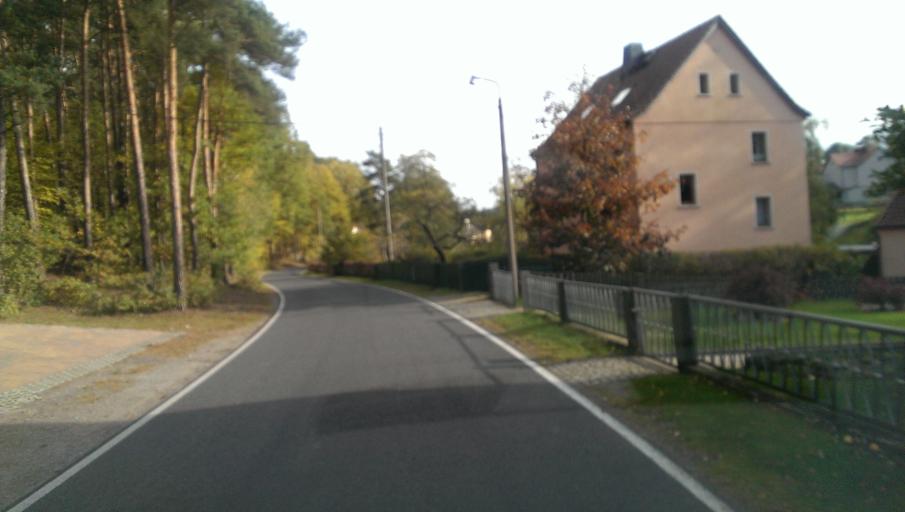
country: DE
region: Saxony
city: Konigsbruck
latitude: 51.2549
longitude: 13.9227
